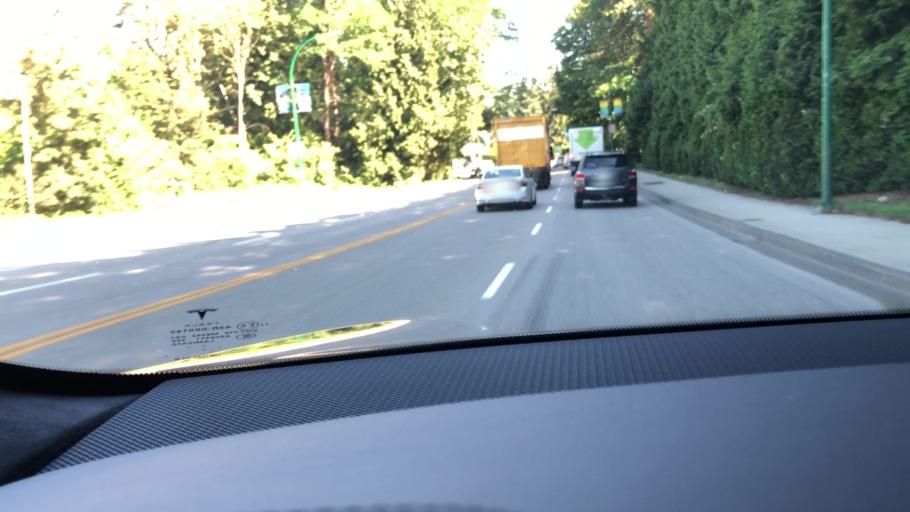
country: CA
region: British Columbia
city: Burnaby
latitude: 49.2408
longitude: -122.9671
